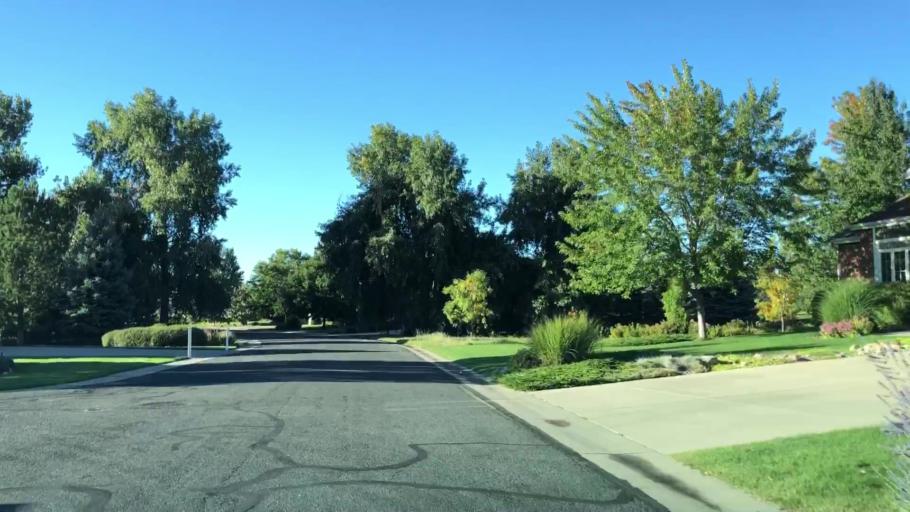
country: US
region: Colorado
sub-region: Larimer County
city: Campion
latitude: 40.3764
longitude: -105.1510
